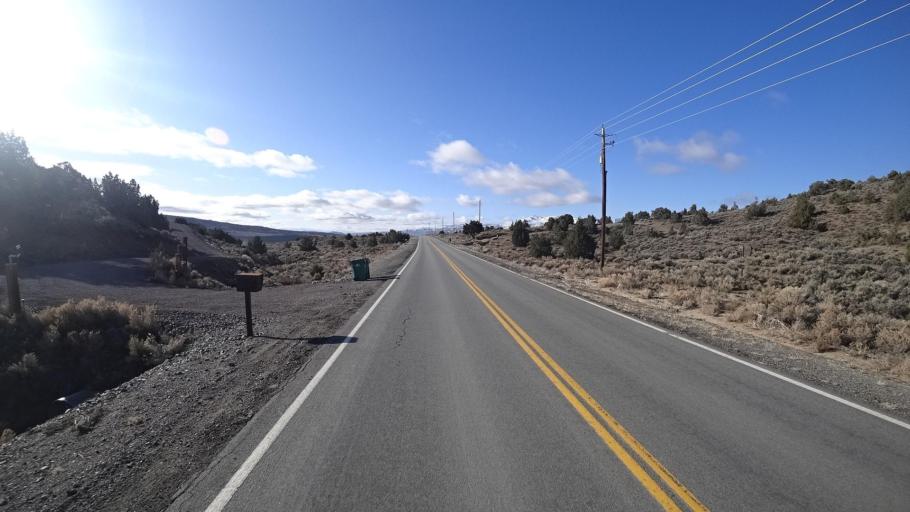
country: US
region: Nevada
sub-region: Washoe County
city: Lemmon Valley
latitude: 39.7291
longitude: -119.8812
